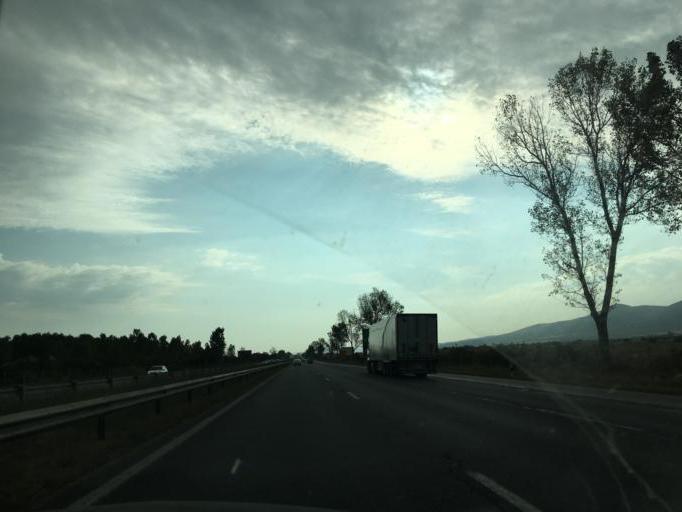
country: BG
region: Sofiya
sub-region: Obshtina Elin Pelin
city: Elin Pelin
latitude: 42.6282
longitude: 23.4864
